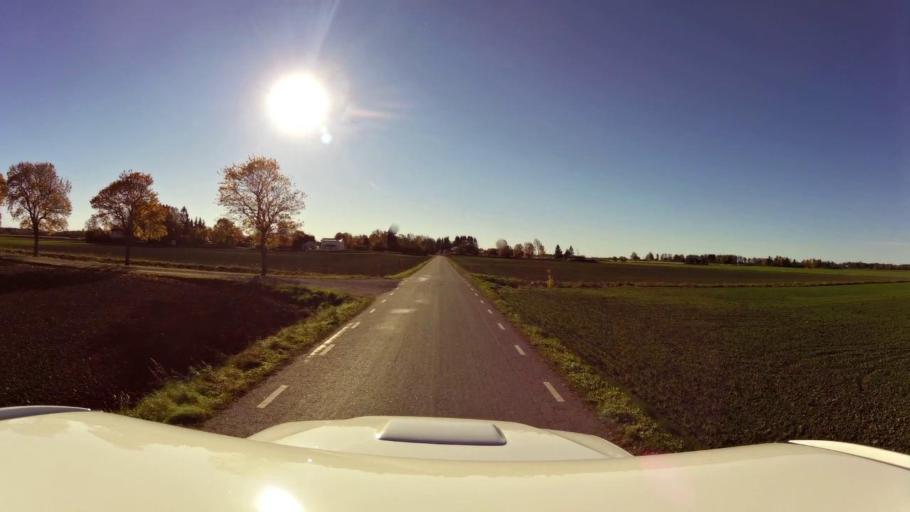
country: SE
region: OEstergoetland
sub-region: Linkopings Kommun
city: Ljungsbro
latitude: 58.4960
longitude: 15.4182
